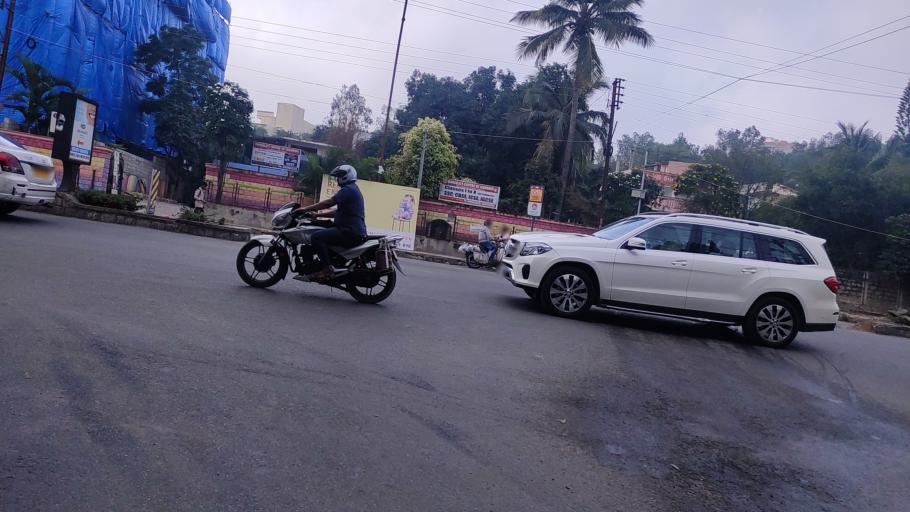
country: IN
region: Telangana
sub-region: Rangareddi
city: Kukatpalli
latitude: 17.4348
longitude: 78.4159
